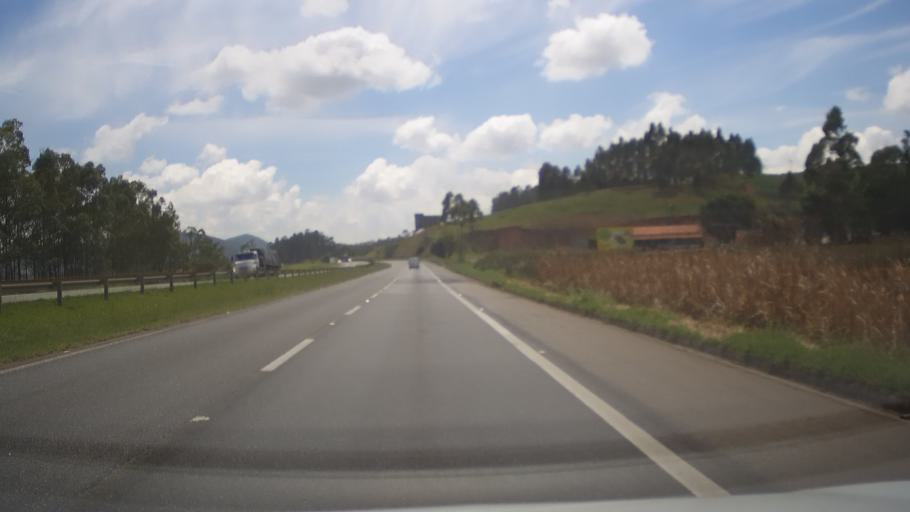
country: BR
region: Minas Gerais
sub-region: Santa Rita Do Sapucai
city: Santa Rita do Sapucai
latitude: -22.0949
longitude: -45.7126
